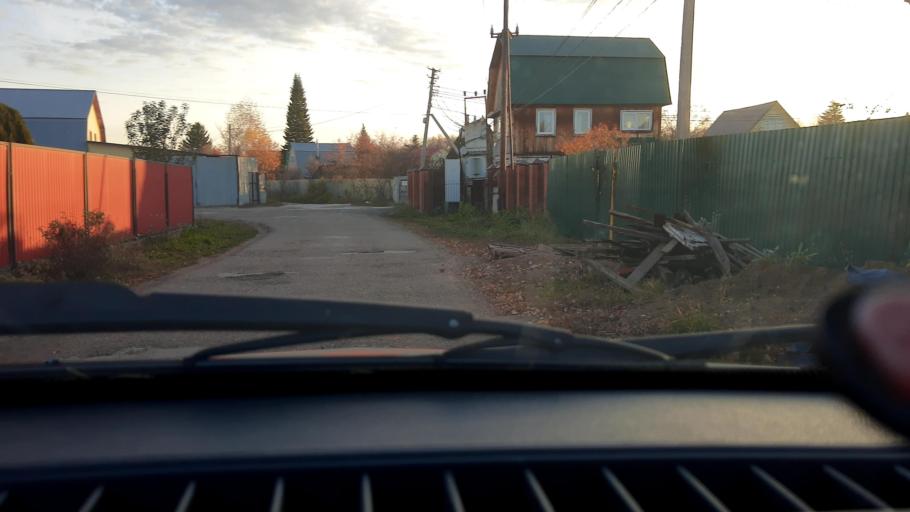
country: RU
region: Bashkortostan
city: Ufa
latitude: 54.6885
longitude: 55.9022
